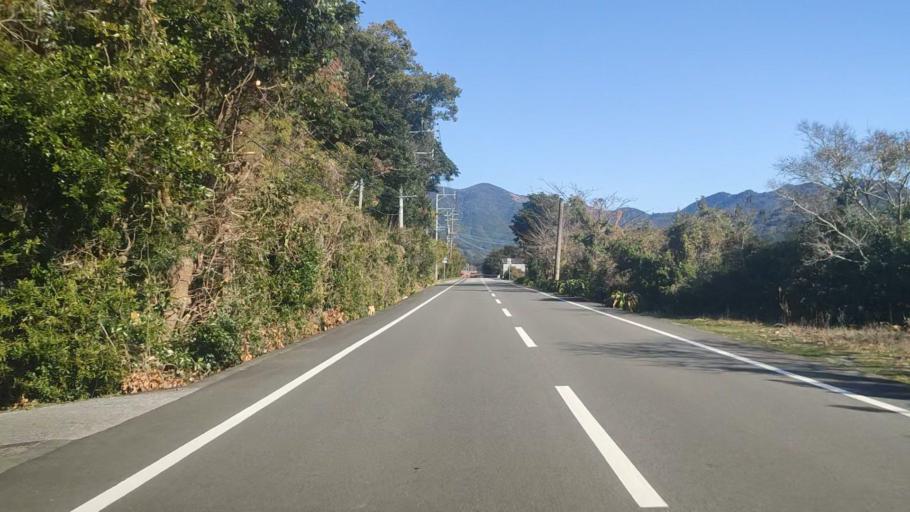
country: JP
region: Oita
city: Saiki
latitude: 32.7987
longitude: 131.8872
